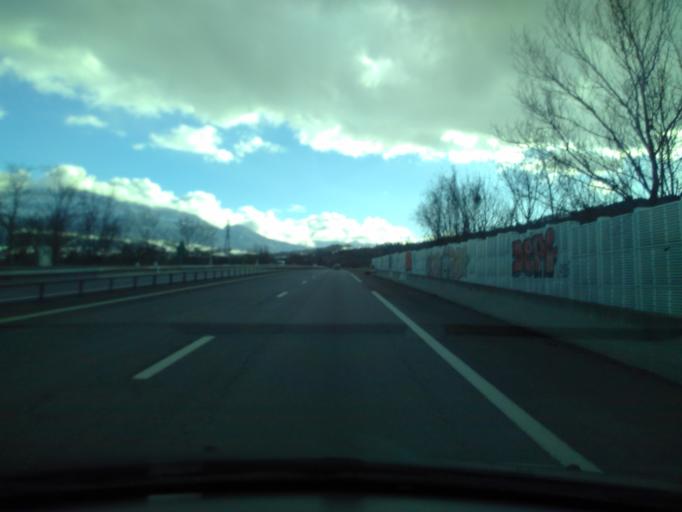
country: FR
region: Rhone-Alpes
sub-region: Departement de la Haute-Savoie
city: Cornier
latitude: 46.0896
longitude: 6.2890
